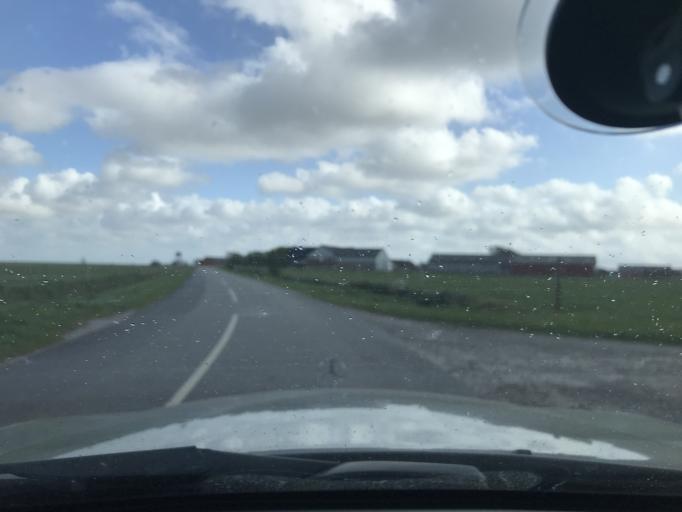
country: DE
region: Schleswig-Holstein
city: List
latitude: 55.1778
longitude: 8.5561
